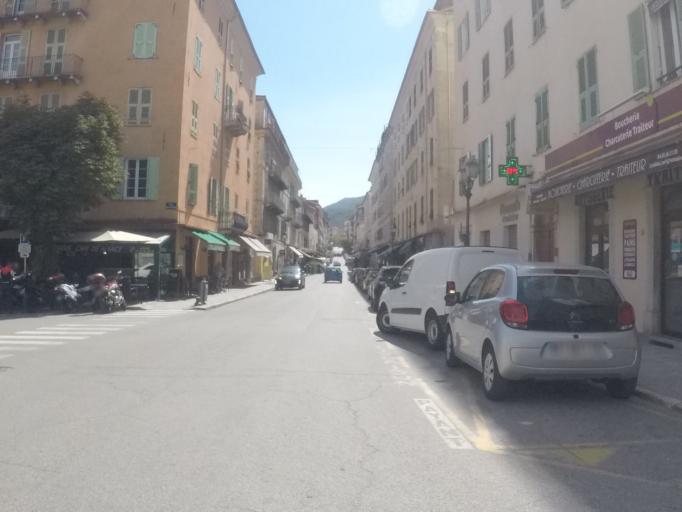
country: FR
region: Corsica
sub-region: Departement de la Haute-Corse
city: Corte
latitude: 42.3084
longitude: 9.1501
